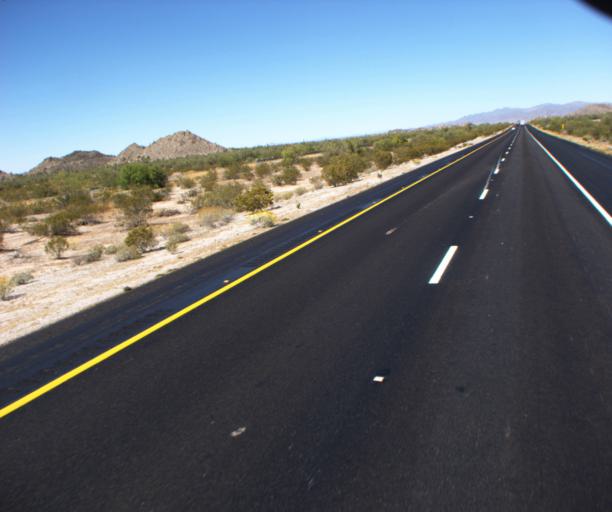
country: US
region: Arizona
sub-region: Maricopa County
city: Buckeye
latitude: 33.2821
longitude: -112.6305
